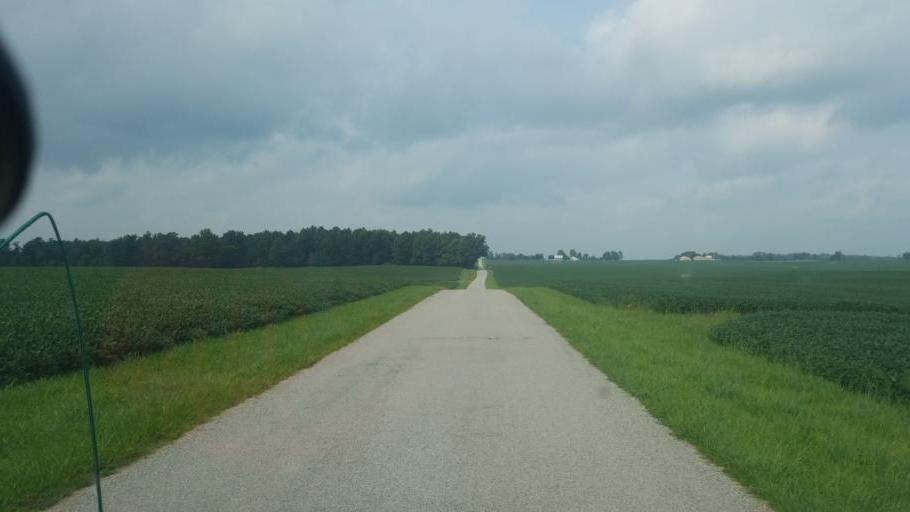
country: US
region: Ohio
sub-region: Huron County
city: New London
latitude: 41.0766
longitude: -82.4618
